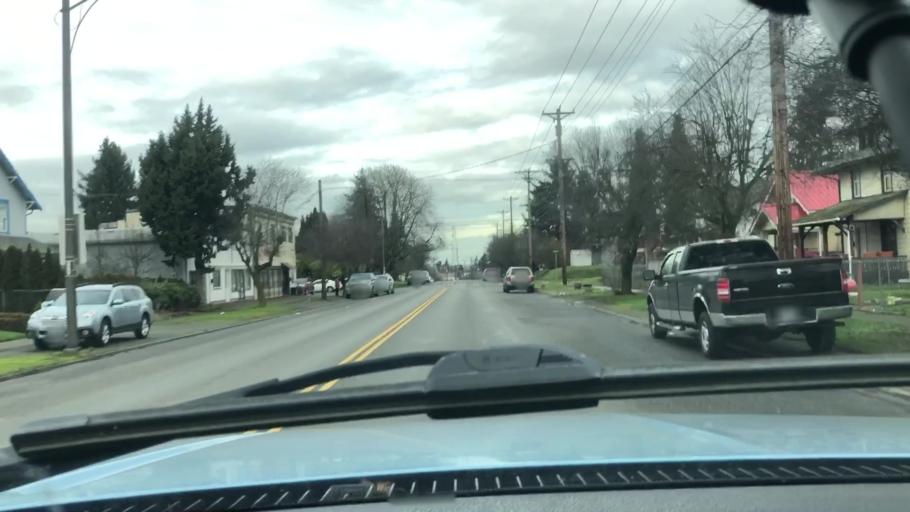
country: US
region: Washington
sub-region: Pierce County
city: Tacoma
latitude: 47.2256
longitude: -122.4208
